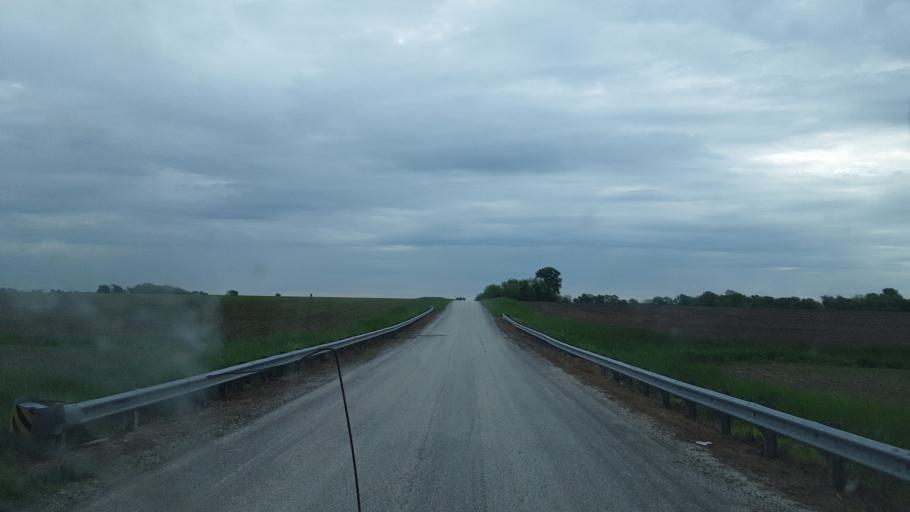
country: US
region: Illinois
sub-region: McDonough County
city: Macomb
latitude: 40.3819
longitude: -90.6559
